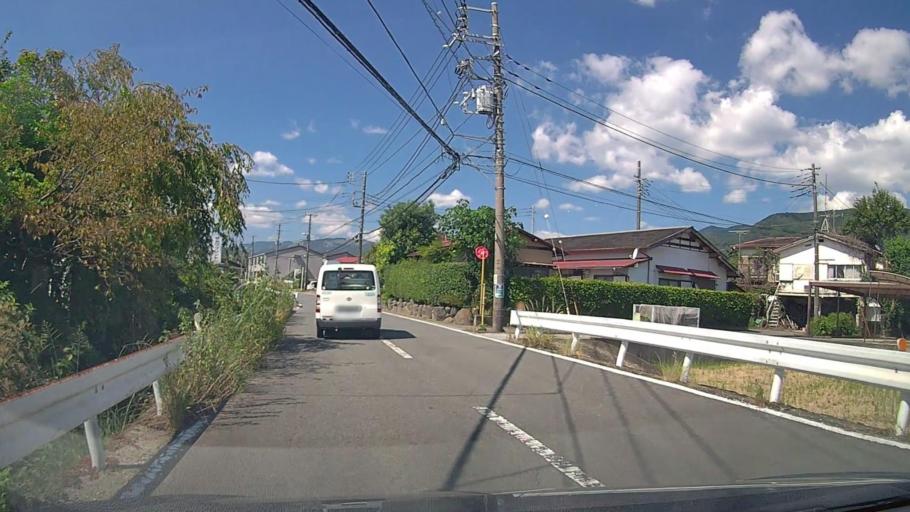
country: JP
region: Kanagawa
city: Odawara
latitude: 35.3410
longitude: 139.1196
